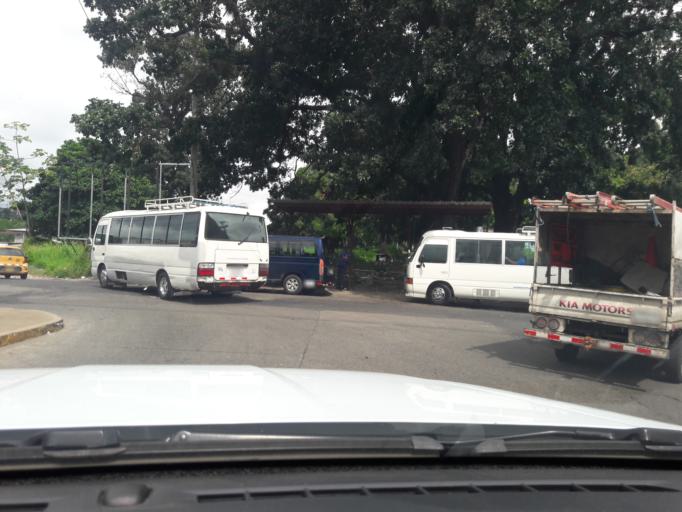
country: PA
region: Panama
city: San Miguelito
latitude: 9.0486
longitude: -79.5056
